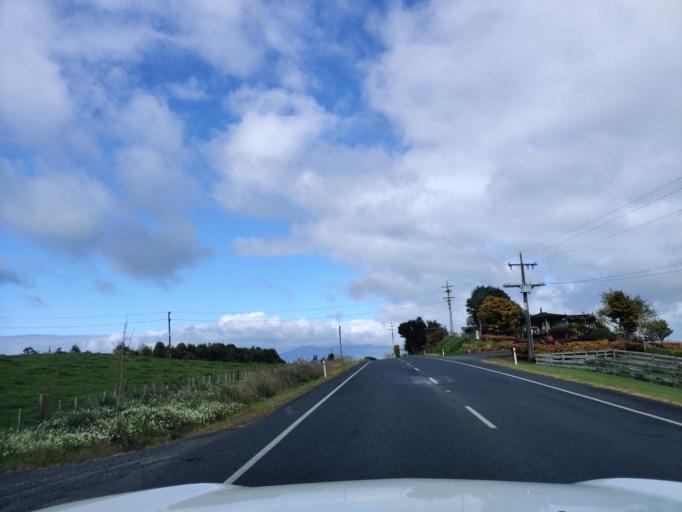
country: NZ
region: Waikato
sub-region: Hamilton City
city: Hamilton
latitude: -37.8396
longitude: 175.2158
